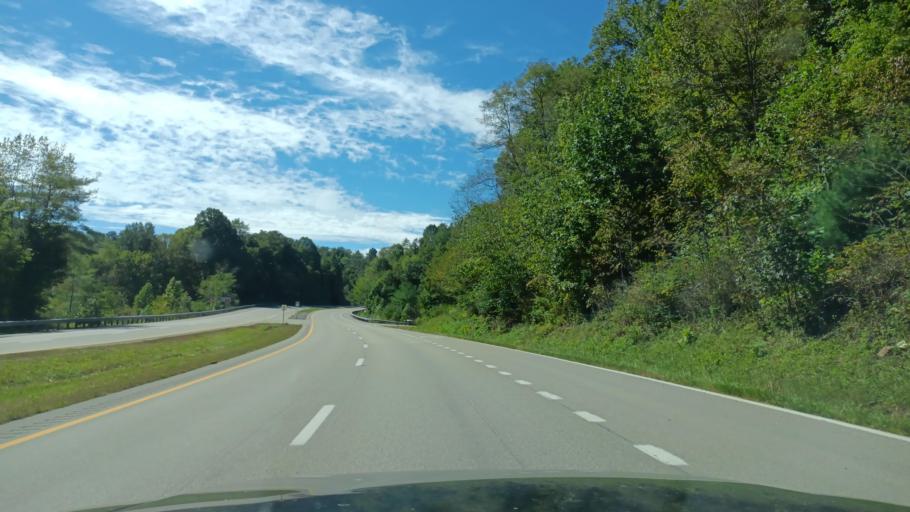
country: US
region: West Virginia
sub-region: Harrison County
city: Salem
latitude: 39.2991
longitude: -80.5831
